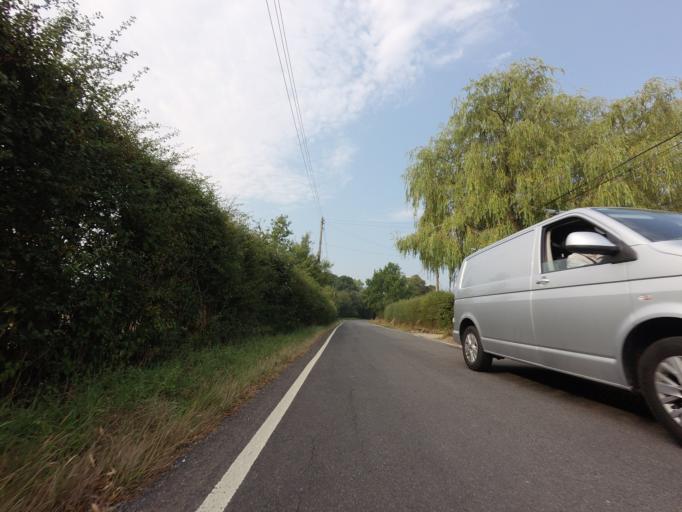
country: GB
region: England
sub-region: Kent
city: Tenterden
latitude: 51.1198
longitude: 0.7083
